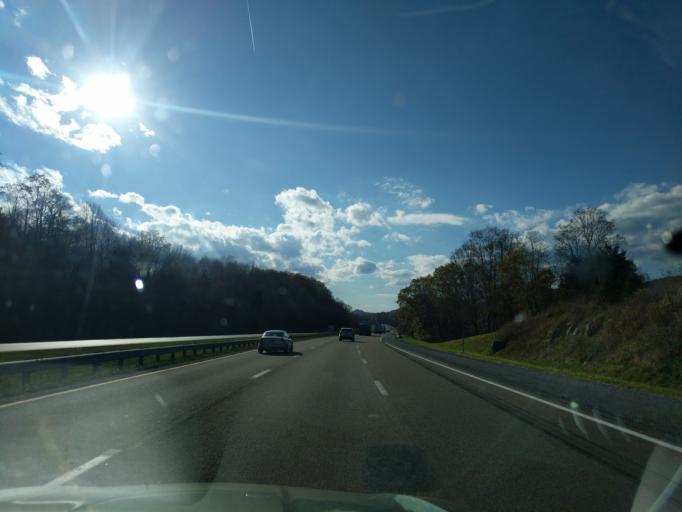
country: US
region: Virginia
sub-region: Wythe County
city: Wytheville
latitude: 36.9379
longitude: -81.1574
